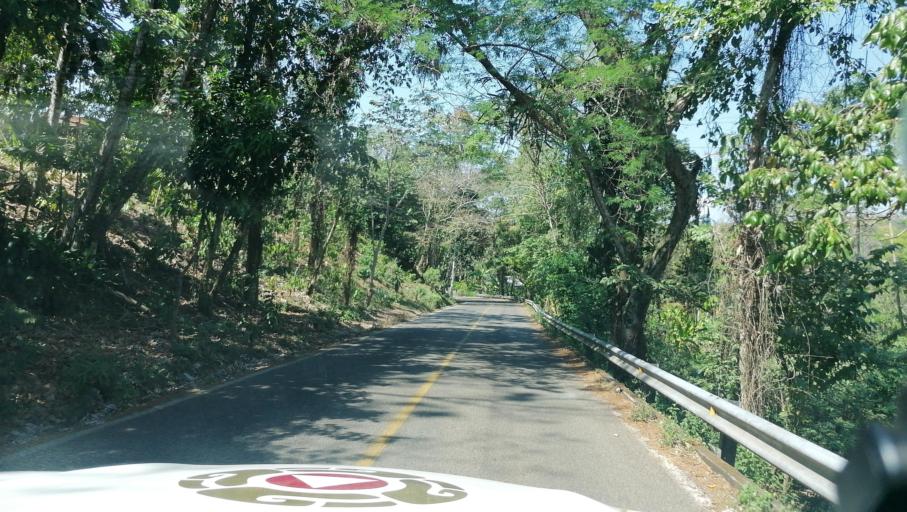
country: MX
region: Chiapas
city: Veinte de Noviembre
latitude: 14.9930
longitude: -92.2368
